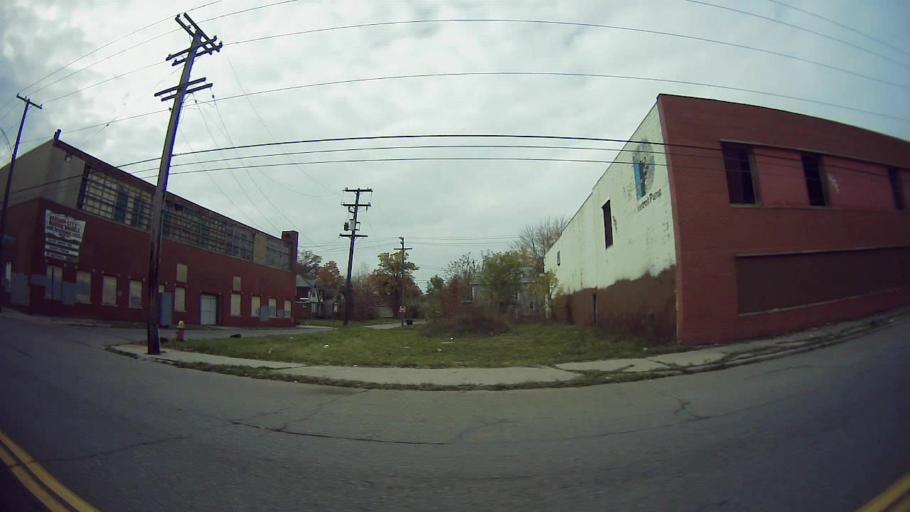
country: US
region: Michigan
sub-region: Wayne County
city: Highland Park
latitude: 42.4308
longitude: -83.1023
